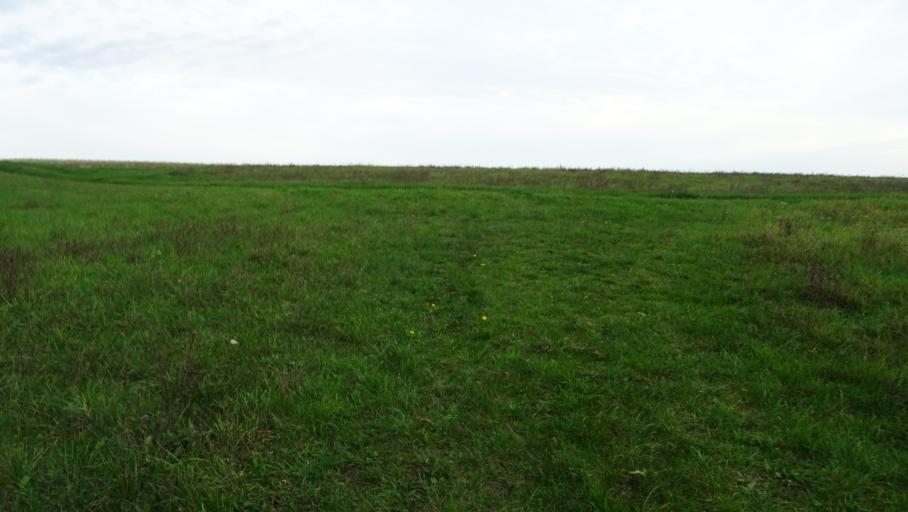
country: DE
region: Baden-Wuerttemberg
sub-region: Karlsruhe Region
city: Binau
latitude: 49.3738
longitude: 9.0672
